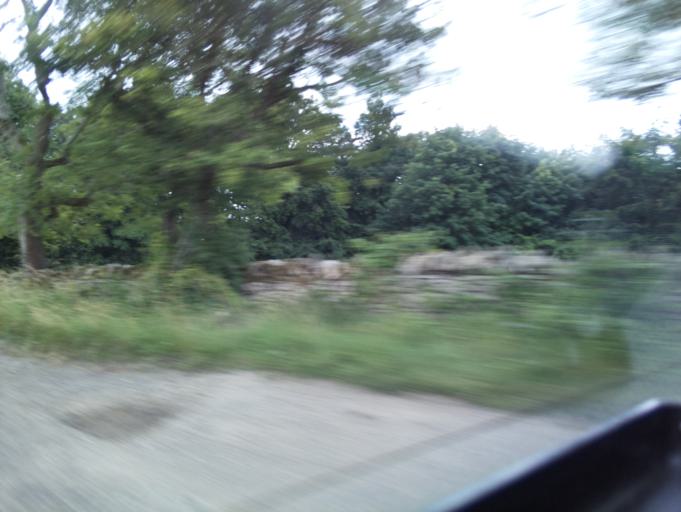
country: GB
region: England
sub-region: Gloucestershire
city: Chalford
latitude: 51.7843
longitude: -2.1098
